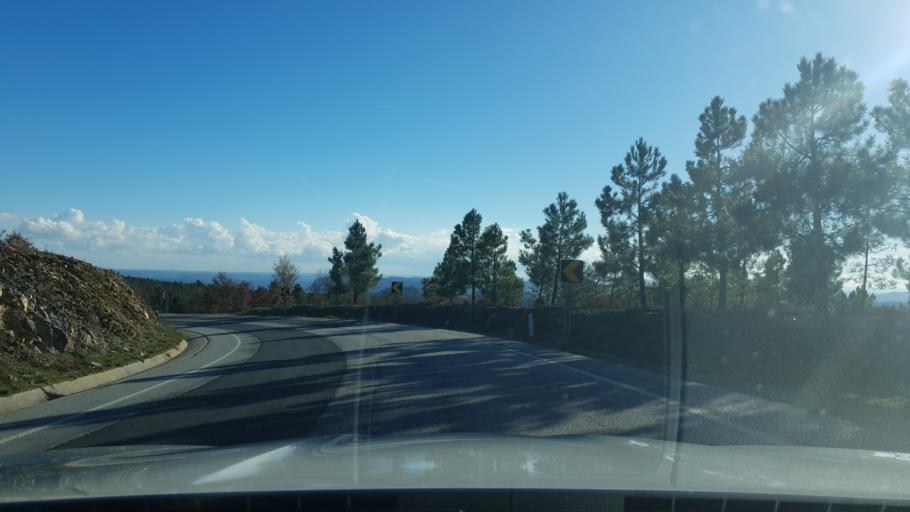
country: PT
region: Braganca
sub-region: Freixo de Espada A Cinta
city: Freixo de Espada a Cinta
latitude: 41.1412
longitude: -6.8087
